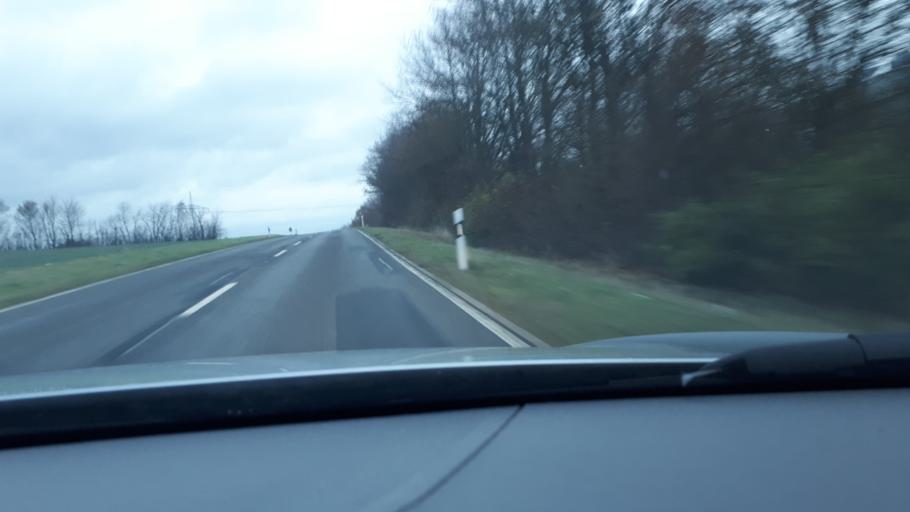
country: DE
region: Rheinland-Pfalz
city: Eulgem
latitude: 50.2402
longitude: 7.1544
